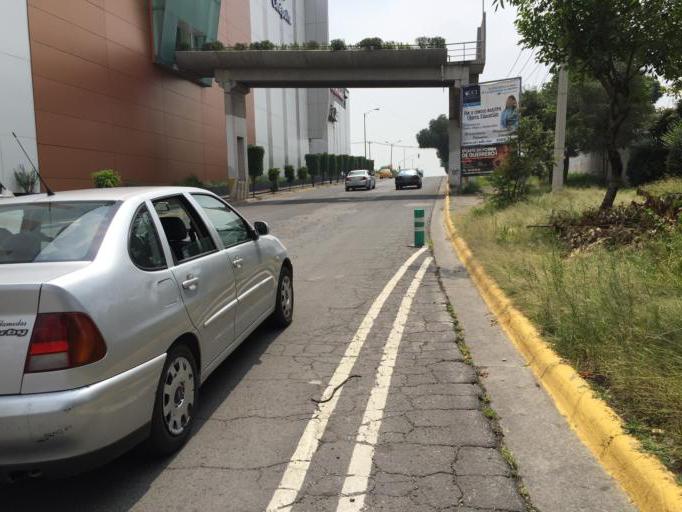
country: MX
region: Mexico
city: Cuautitlan Izcalli
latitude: 19.6568
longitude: -99.2109
